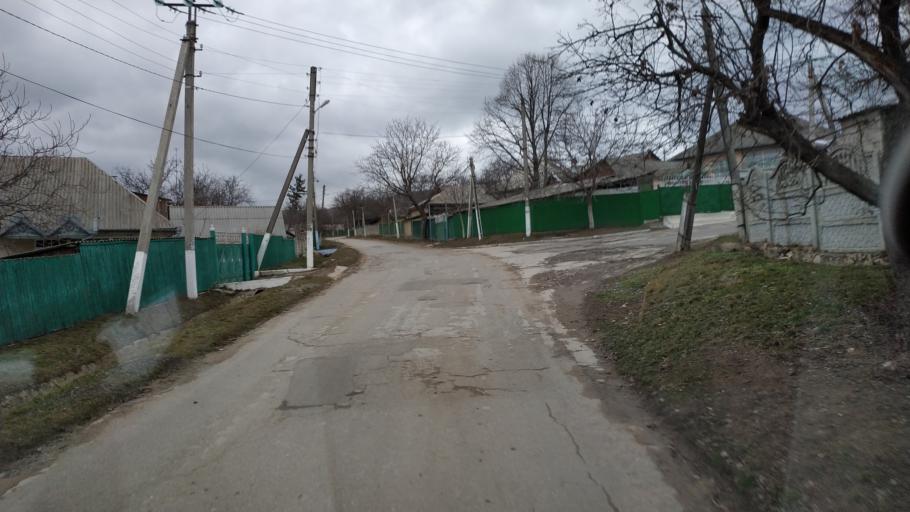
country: MD
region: Calarasi
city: Calarasi
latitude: 47.2066
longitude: 28.2515
